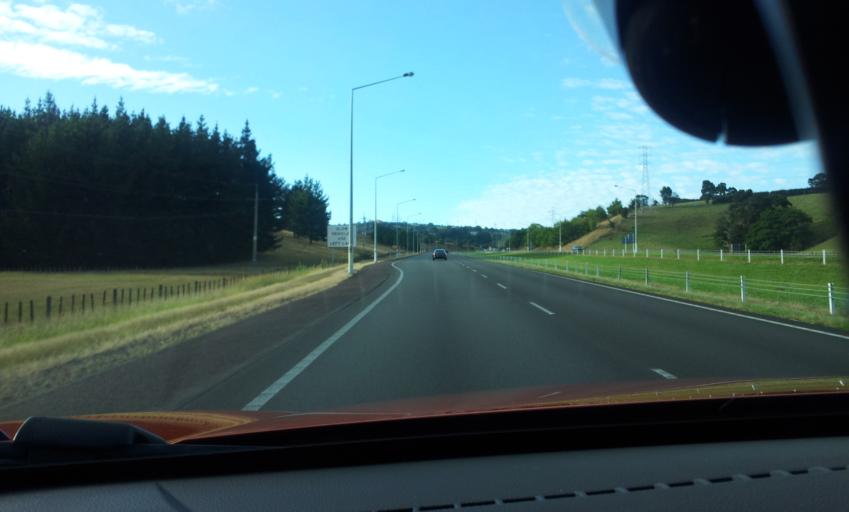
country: NZ
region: Auckland
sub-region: Auckland
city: Pukekohe East
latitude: -37.1603
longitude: 174.9803
